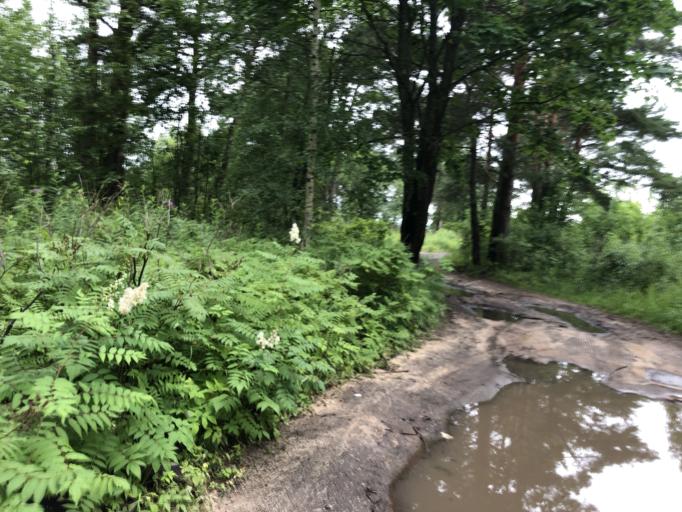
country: RU
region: Tverskaya
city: Rzhev
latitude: 56.2431
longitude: 34.3757
